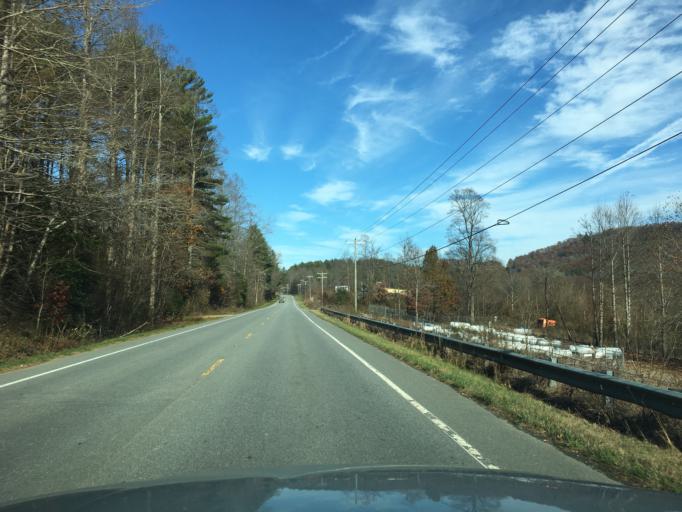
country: US
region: North Carolina
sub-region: Henderson County
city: Etowah
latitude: 35.2812
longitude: -82.6294
